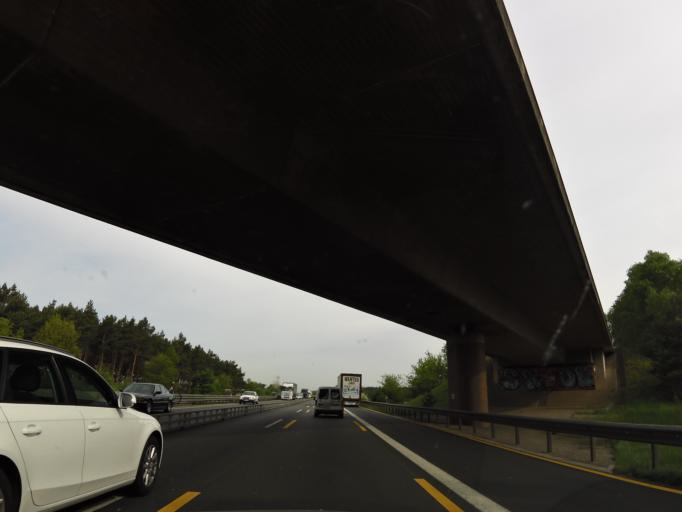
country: DE
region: Lower Saxony
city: Essel
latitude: 52.7153
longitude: 9.6827
